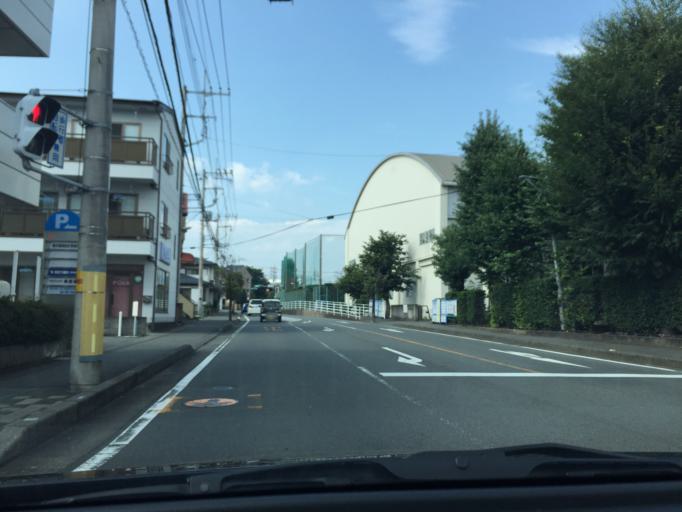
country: JP
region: Shizuoka
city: Mishima
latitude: 35.1320
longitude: 138.8985
